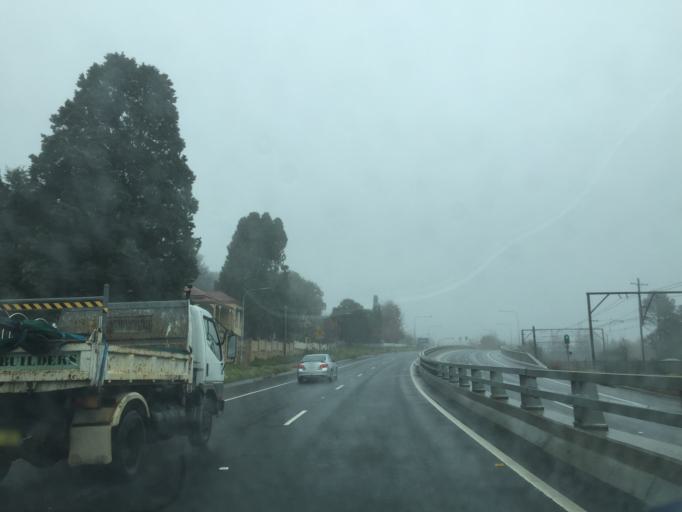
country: AU
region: New South Wales
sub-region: Blue Mountains Municipality
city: Leura
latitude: -33.7129
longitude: 150.3781
